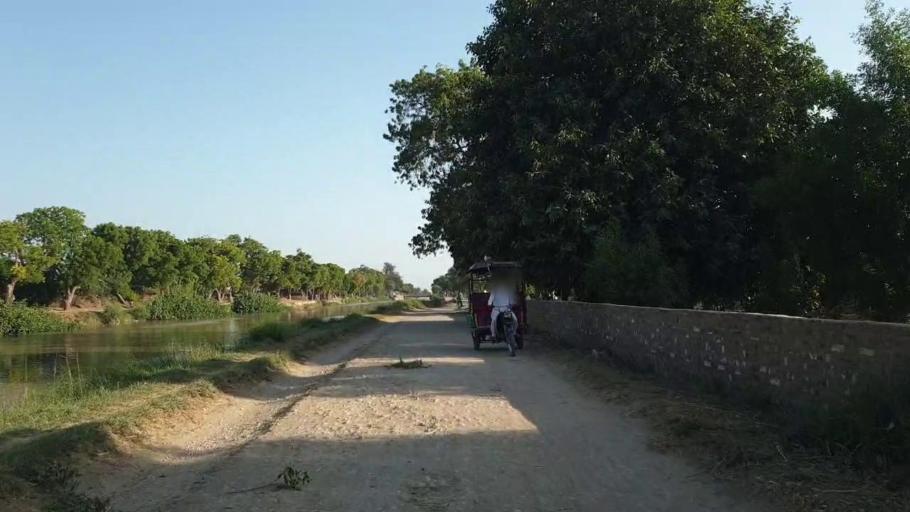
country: PK
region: Sindh
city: Hyderabad
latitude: 25.3195
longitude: 68.4282
